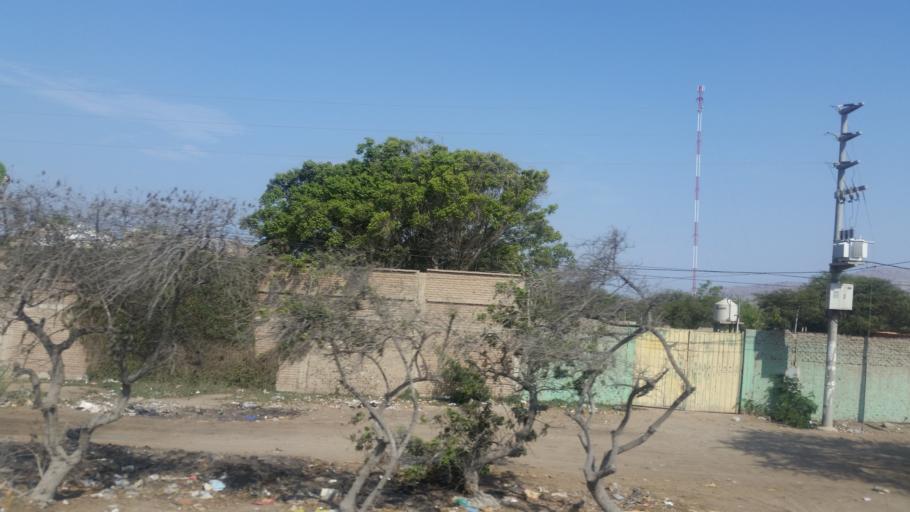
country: PE
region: Lambayeque
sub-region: Provincia de Chiclayo
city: Reque
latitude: -6.8266
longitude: -79.8294
